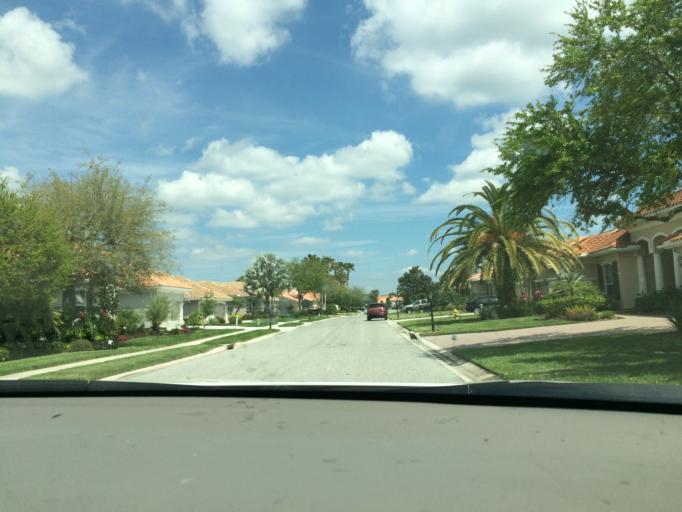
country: US
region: Florida
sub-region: Manatee County
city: Ellenton
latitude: 27.5148
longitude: -82.4356
